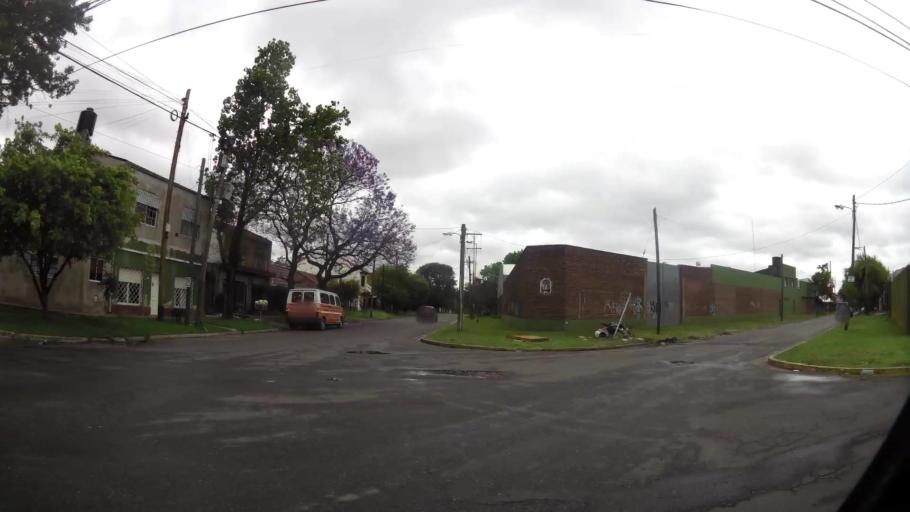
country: AR
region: Buenos Aires
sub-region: Partido de Lomas de Zamora
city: Lomas de Zamora
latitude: -34.7453
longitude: -58.3751
